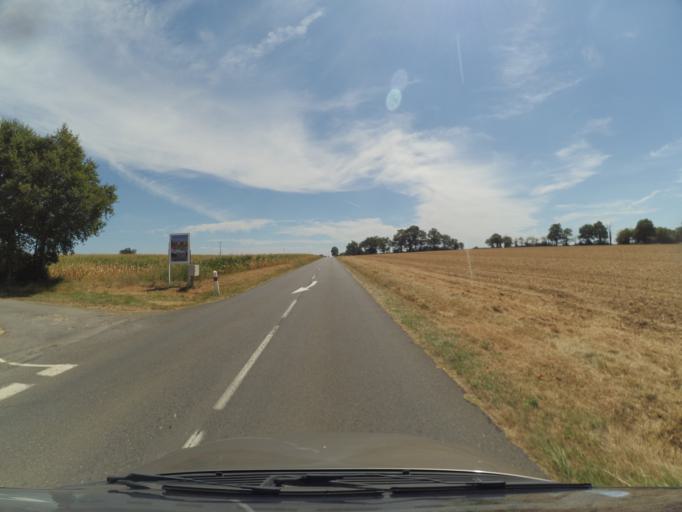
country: FR
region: Poitou-Charentes
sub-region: Departement de la Vienne
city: Usson-du-Poitou
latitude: 46.1928
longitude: 0.5380
